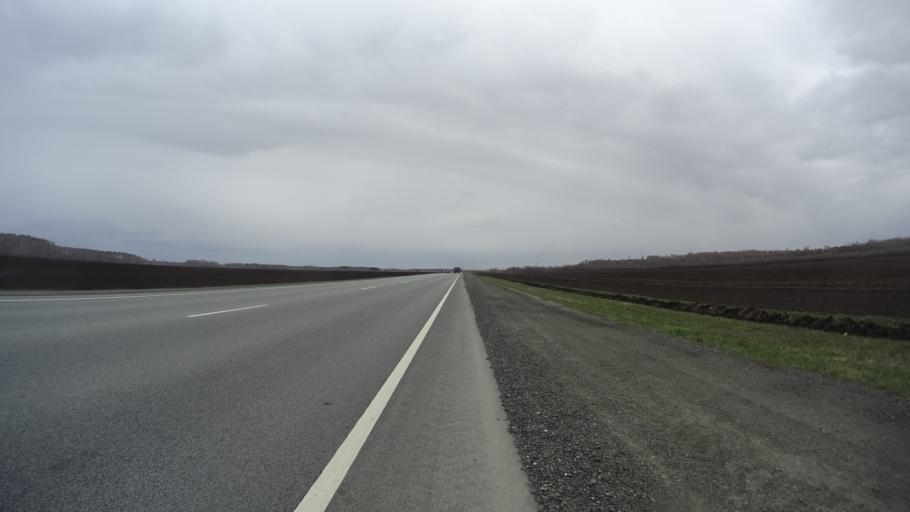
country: RU
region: Chelyabinsk
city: Krasnogorskiy
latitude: 54.5739
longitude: 61.2910
